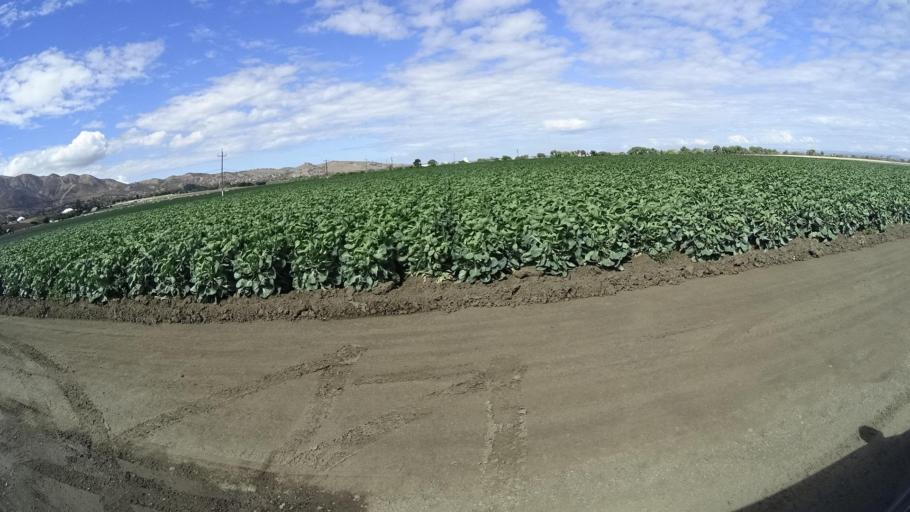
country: US
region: California
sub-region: Monterey County
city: Salinas
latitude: 36.6004
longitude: -121.6095
